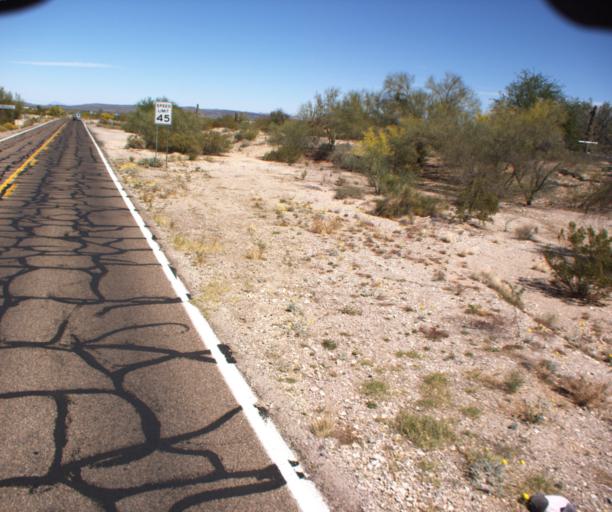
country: US
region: Arizona
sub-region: Pima County
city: Ajo
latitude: 32.3968
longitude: -112.8720
